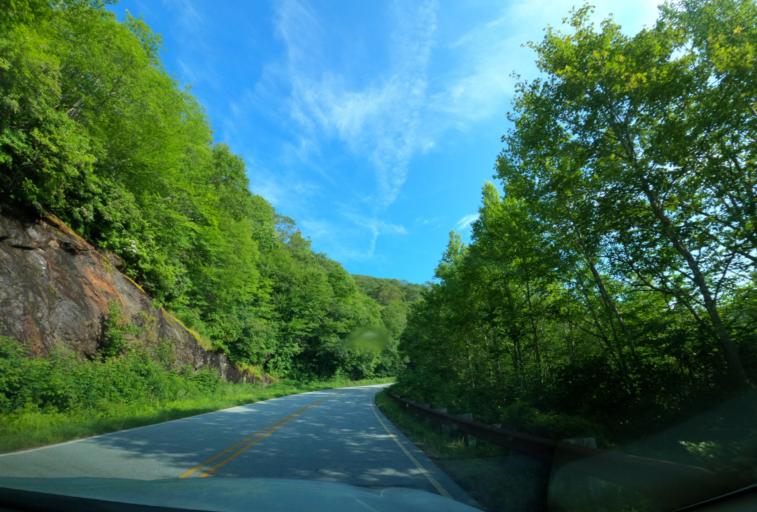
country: US
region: North Carolina
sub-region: Transylvania County
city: Brevard
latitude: 35.2801
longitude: -82.9190
